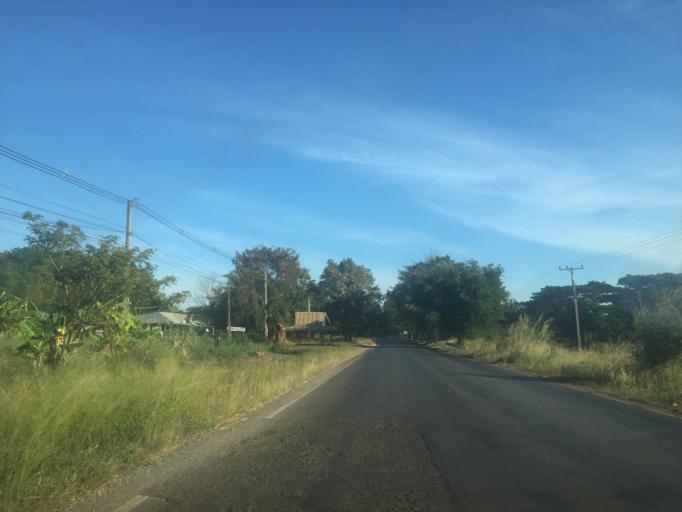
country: TH
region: Kalasin
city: Tha Khantho
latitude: 16.9653
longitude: 103.2460
